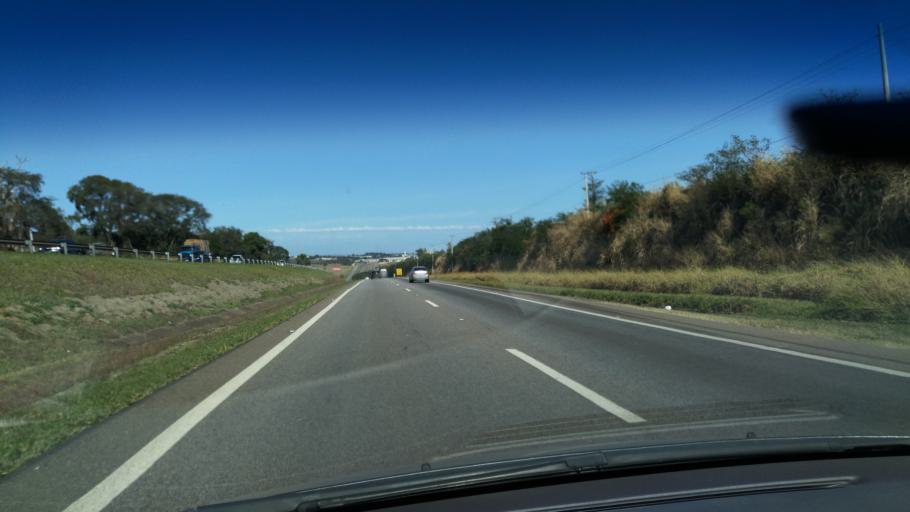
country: BR
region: Sao Paulo
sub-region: Jaguariuna
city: Jaguariuna
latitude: -22.6475
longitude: -47.0057
